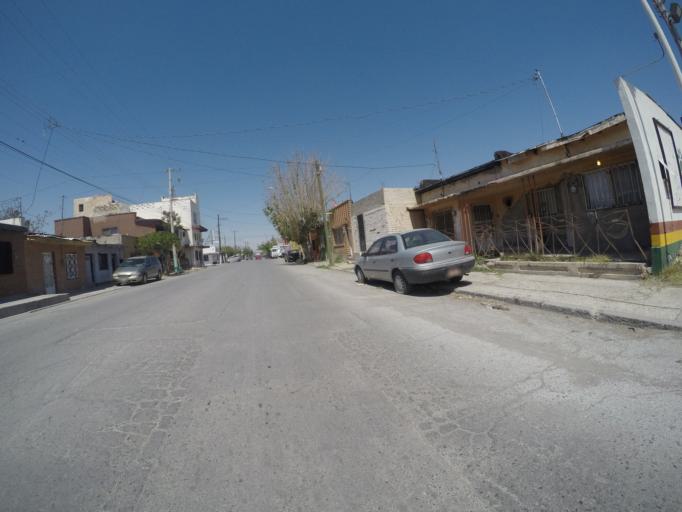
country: MX
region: Chihuahua
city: Ciudad Juarez
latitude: 31.7278
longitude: -106.4806
